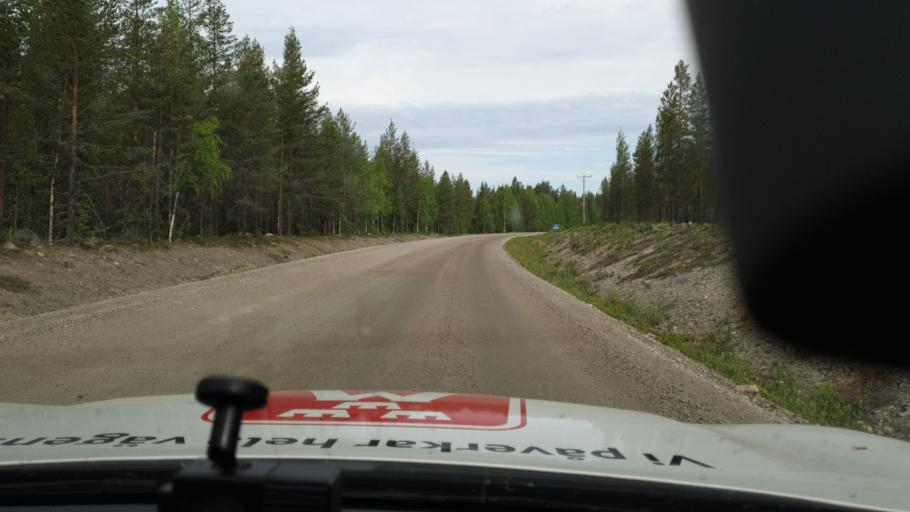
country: SE
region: Vaesterbotten
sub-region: Lycksele Kommun
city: Lycksele
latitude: 64.8596
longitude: 18.7265
